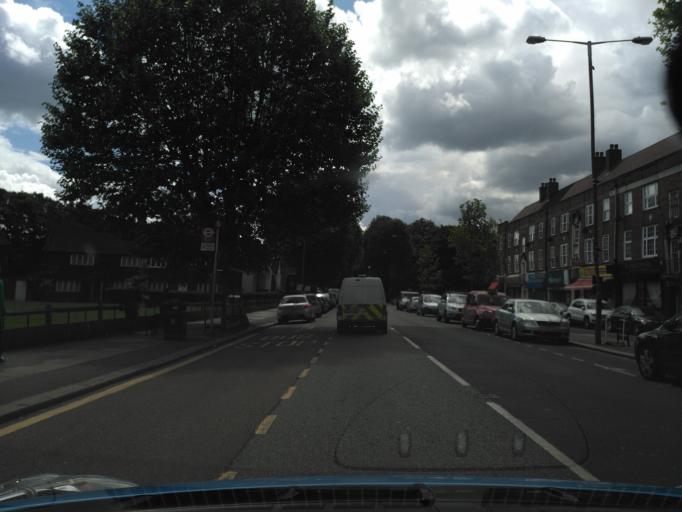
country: GB
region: England
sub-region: Greater London
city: Woolwich
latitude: 51.4584
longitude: 0.0500
